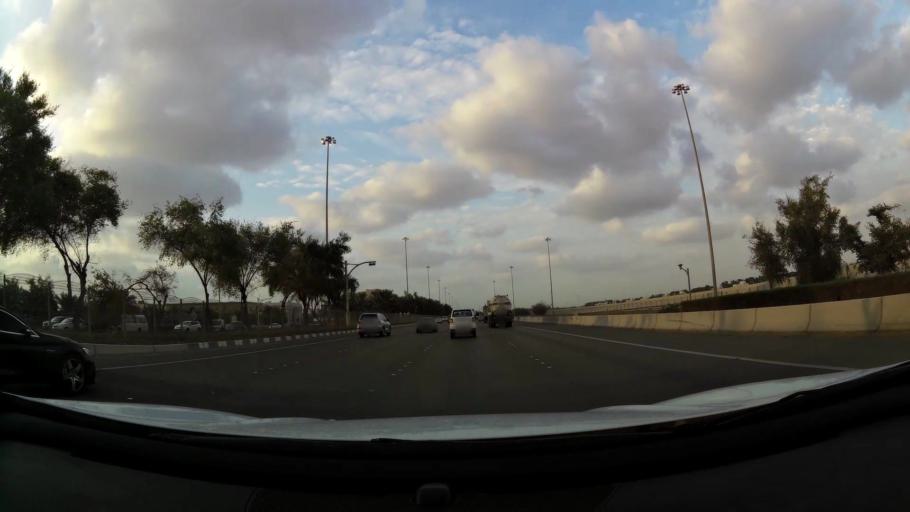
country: AE
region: Abu Dhabi
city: Abu Dhabi
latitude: 24.3755
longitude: 54.5249
